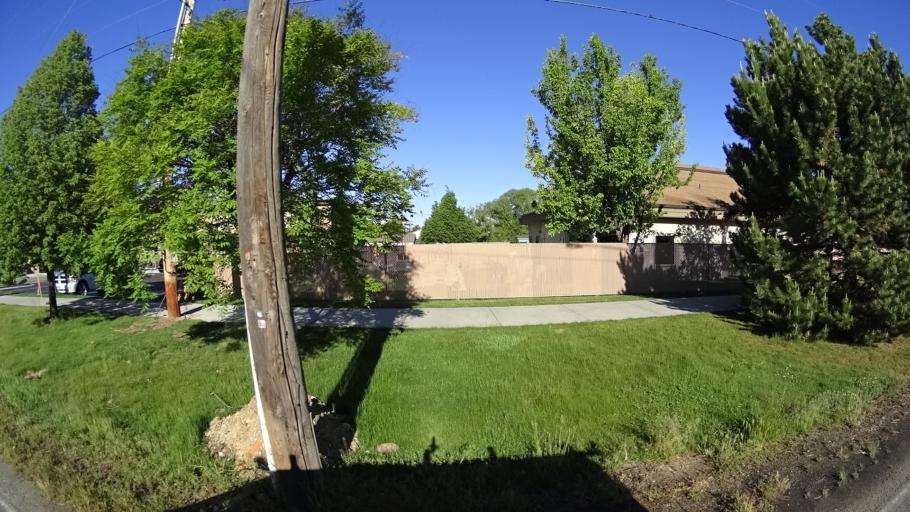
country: US
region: Idaho
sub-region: Ada County
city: Kuna
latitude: 43.5043
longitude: -116.4138
